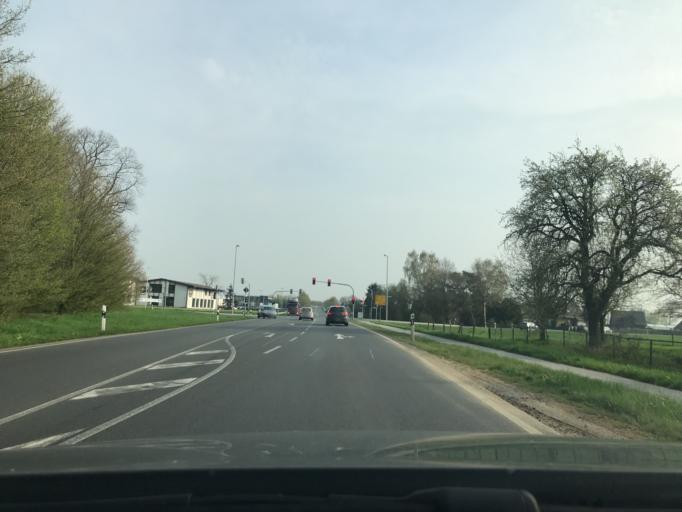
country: DE
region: North Rhine-Westphalia
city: Geldern
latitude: 51.5233
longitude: 6.2877
